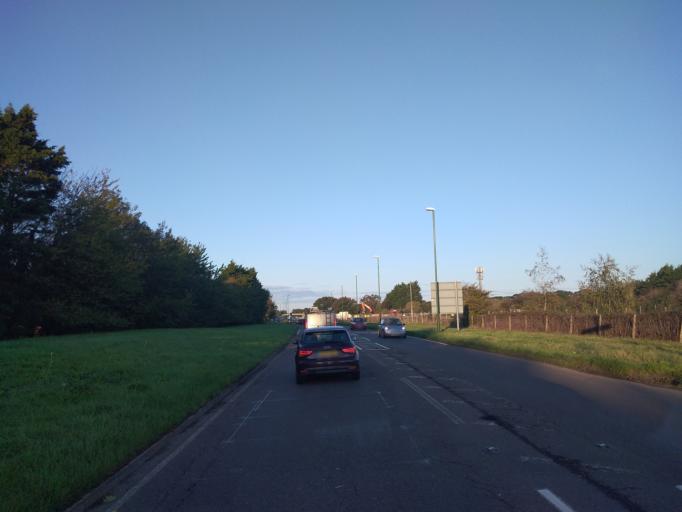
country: GB
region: England
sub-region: West Sussex
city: Rustington
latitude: 50.8183
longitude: -0.4782
